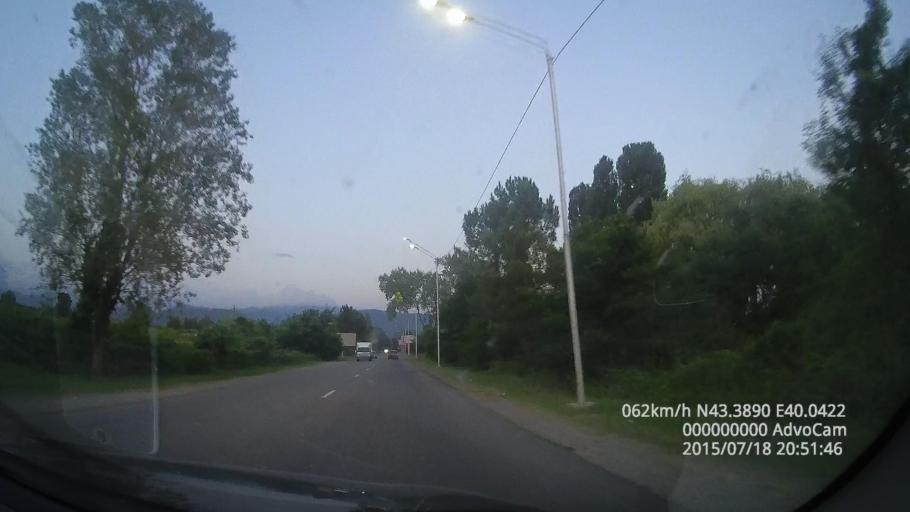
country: GE
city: Gantiadi
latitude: 43.3887
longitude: 40.0437
